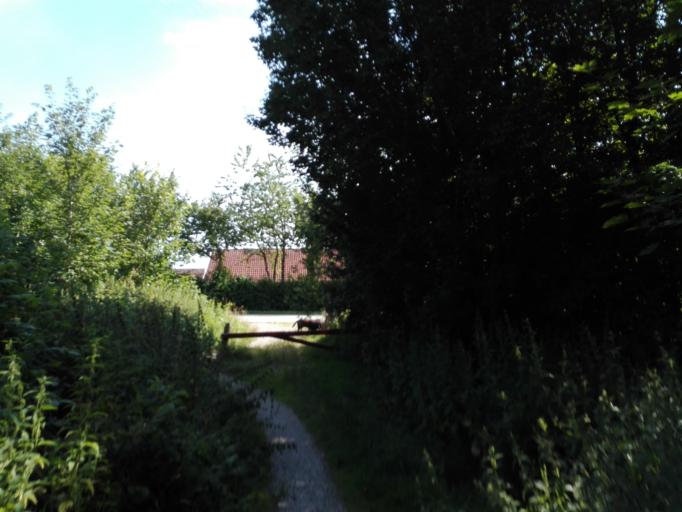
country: DK
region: Central Jutland
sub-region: Arhus Kommune
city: Tranbjerg
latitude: 56.0992
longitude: 10.1214
